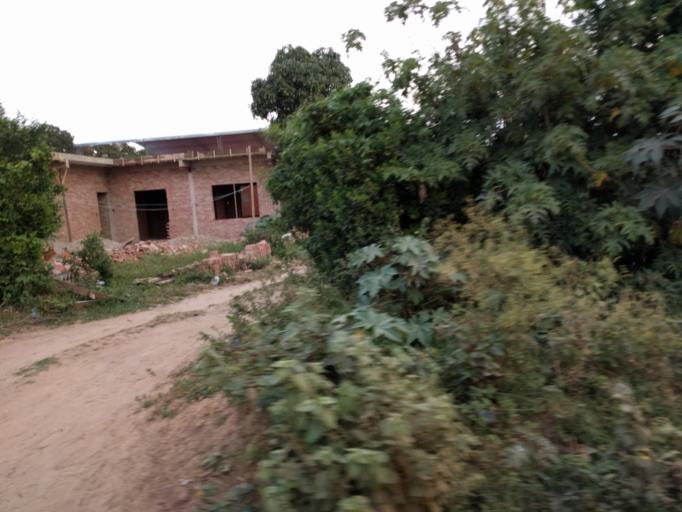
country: BO
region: Santa Cruz
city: Santa Rita
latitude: -17.9472
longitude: -63.3547
